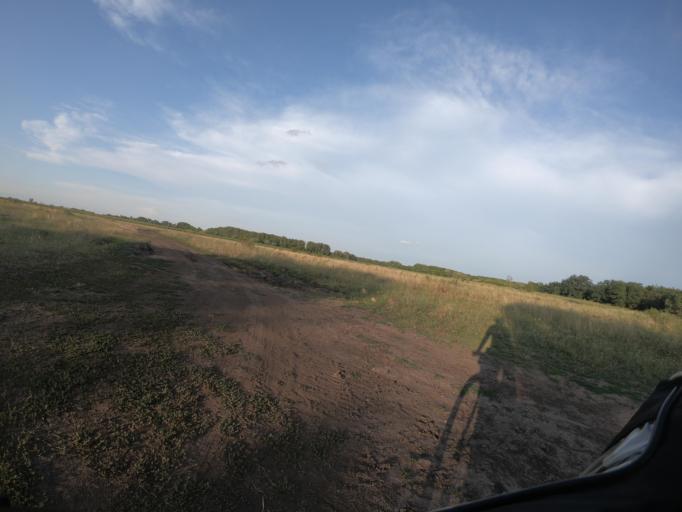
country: HU
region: Borsod-Abauj-Zemplen
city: Mezokeresztes
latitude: 47.7673
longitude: 20.7765
